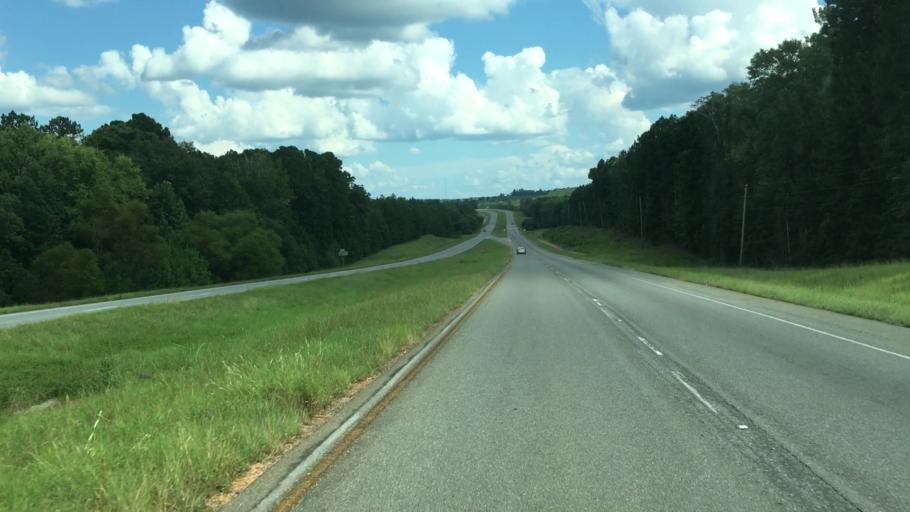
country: US
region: Georgia
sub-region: Wilkinson County
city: Irwinton
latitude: 32.7046
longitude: -83.1282
